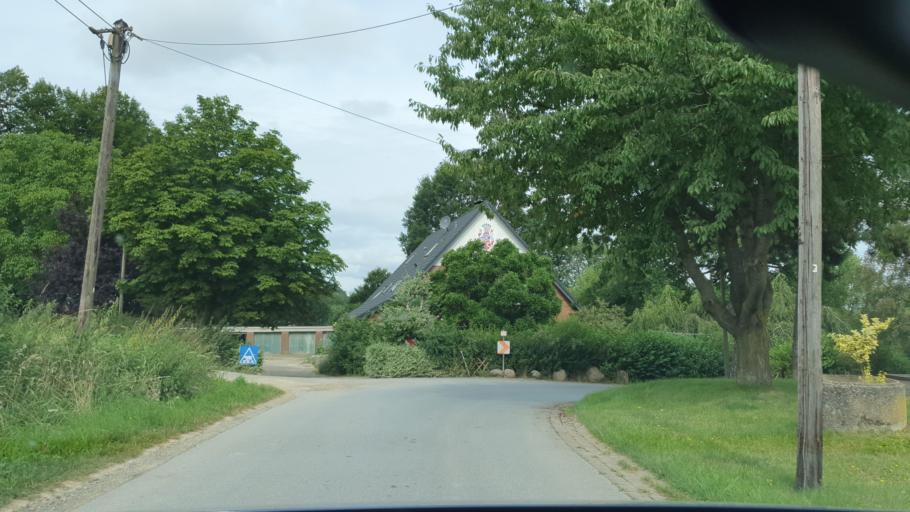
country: DE
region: North Rhine-Westphalia
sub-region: Regierungsbezirk Detmold
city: Werther
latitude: 52.0887
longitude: 8.4114
